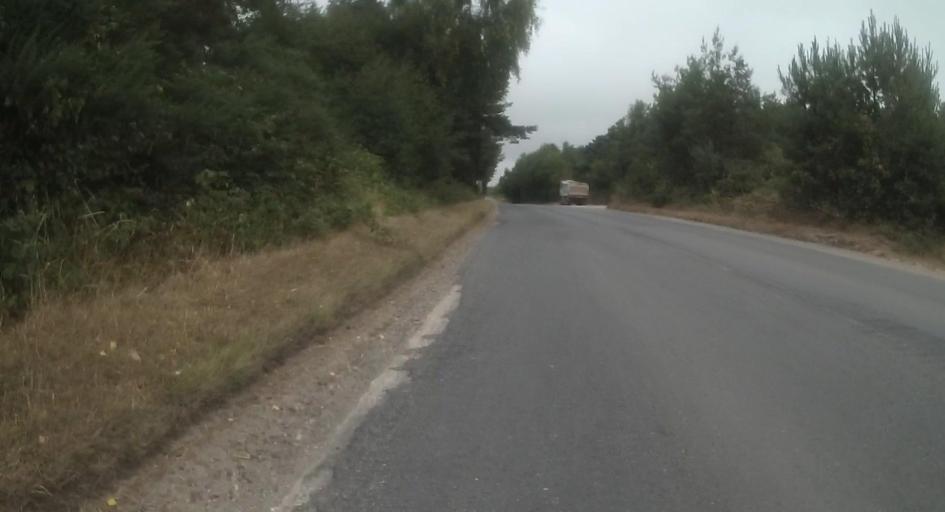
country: GB
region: England
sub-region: Dorset
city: Wool
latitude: 50.7065
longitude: -2.2034
